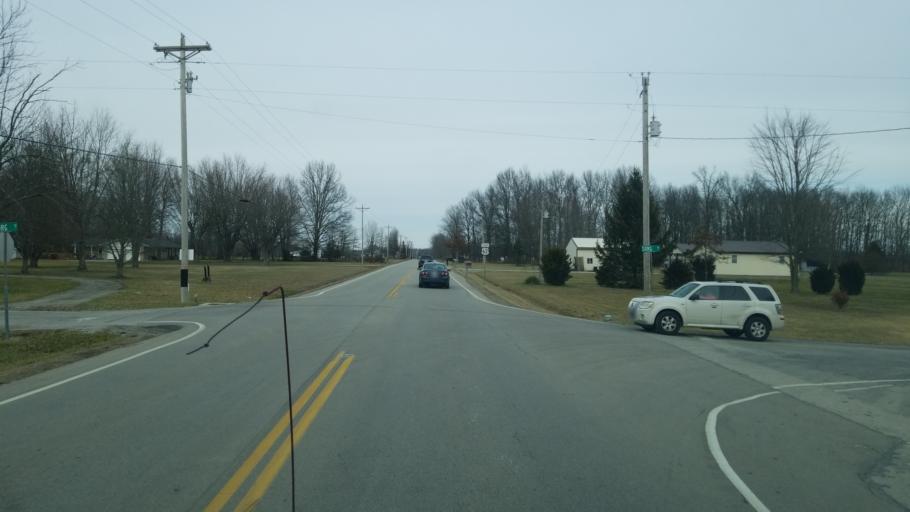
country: US
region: Ohio
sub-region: Highland County
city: Hillsboro
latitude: 39.0866
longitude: -83.6825
